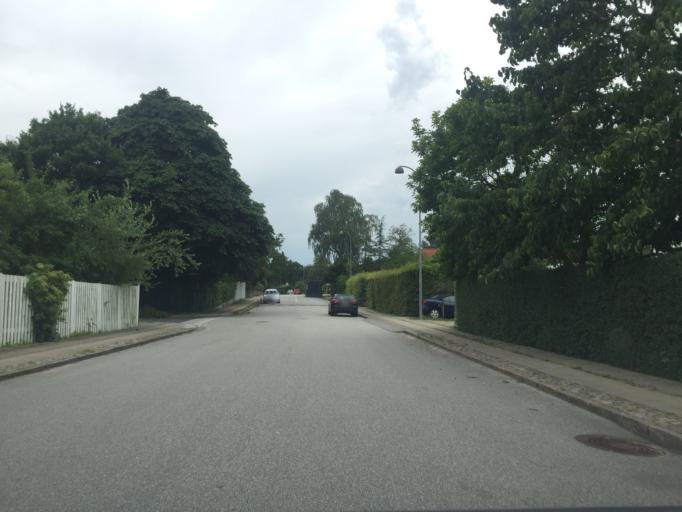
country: DK
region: Capital Region
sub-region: Gentofte Kommune
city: Charlottenlund
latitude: 55.7683
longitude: 12.5525
